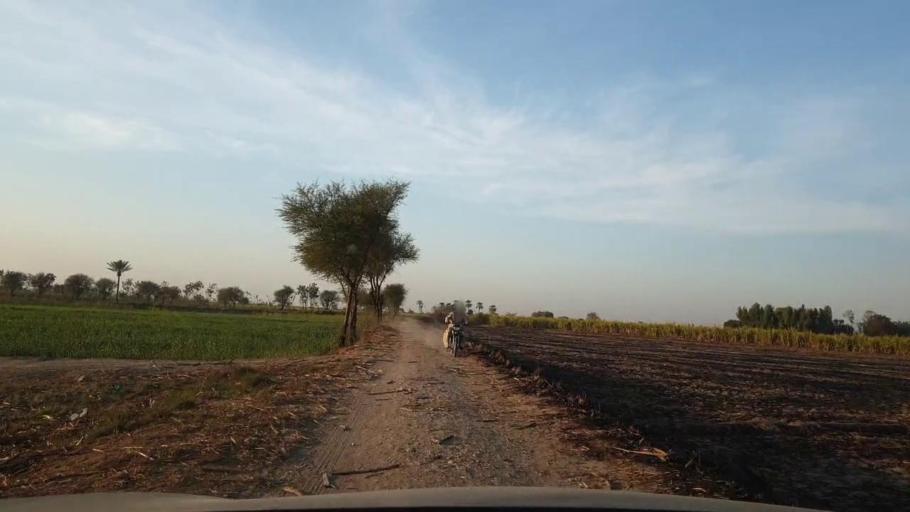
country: PK
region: Sindh
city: Tando Adam
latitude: 25.6136
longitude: 68.6814
